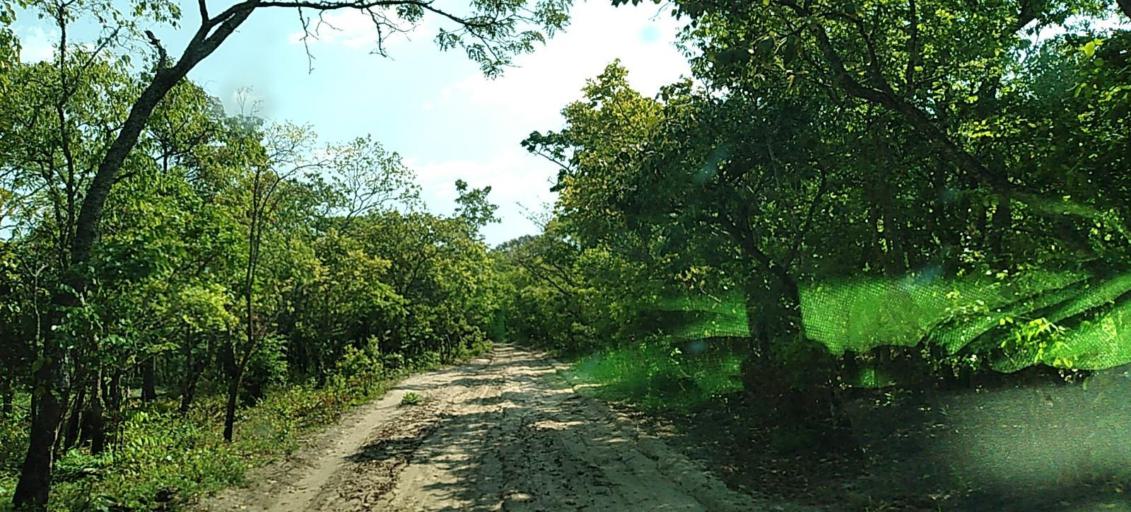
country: ZM
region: North-Western
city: Mwinilunga
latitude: -11.2782
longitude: 24.9272
